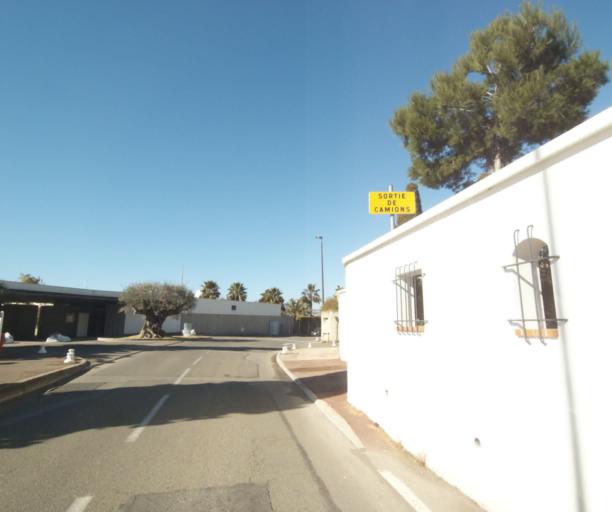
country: FR
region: Provence-Alpes-Cote d'Azur
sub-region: Departement des Alpes-Maritimes
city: Antibes
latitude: 43.5615
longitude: 7.1187
